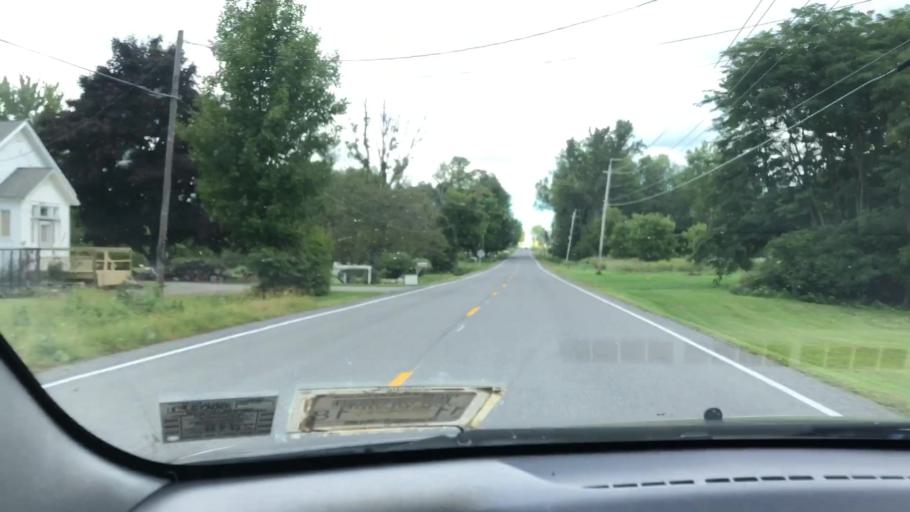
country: US
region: New York
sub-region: Wayne County
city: Macedon
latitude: 43.0972
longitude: -77.3206
